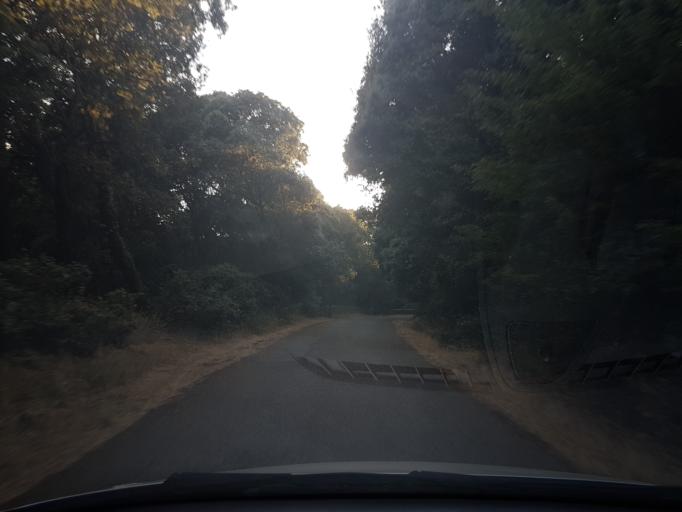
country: IT
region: Sardinia
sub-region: Provincia di Oristano
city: Seneghe
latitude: 40.1144
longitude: 8.5774
